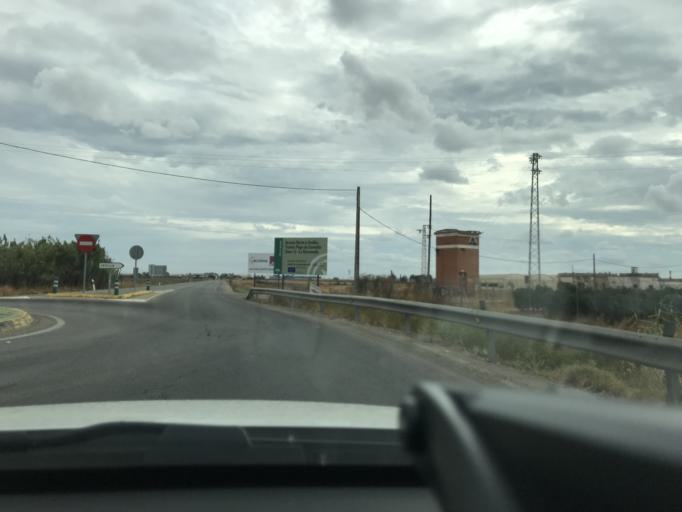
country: ES
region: Andalusia
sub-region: Provincia de Sevilla
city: La Rinconada
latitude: 37.4678
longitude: -5.9716
